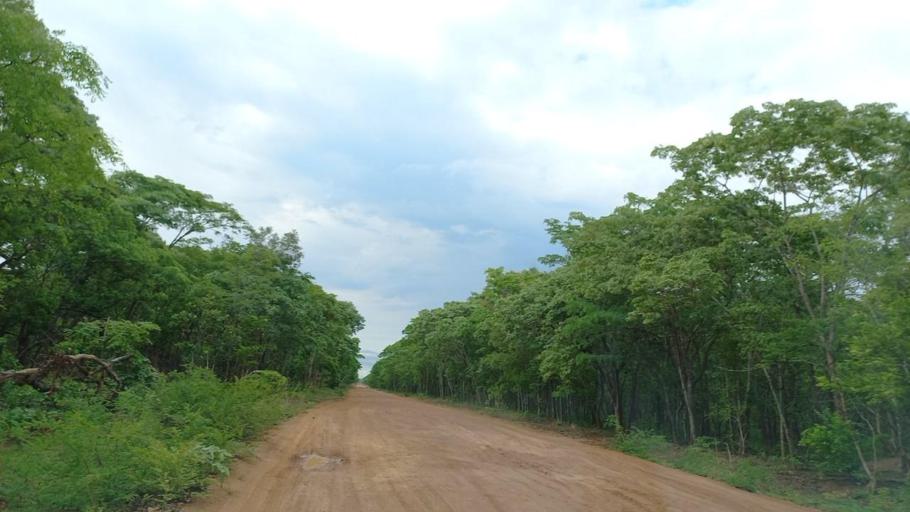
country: ZM
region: North-Western
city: Kalengwa
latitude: -13.3652
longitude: 25.0750
